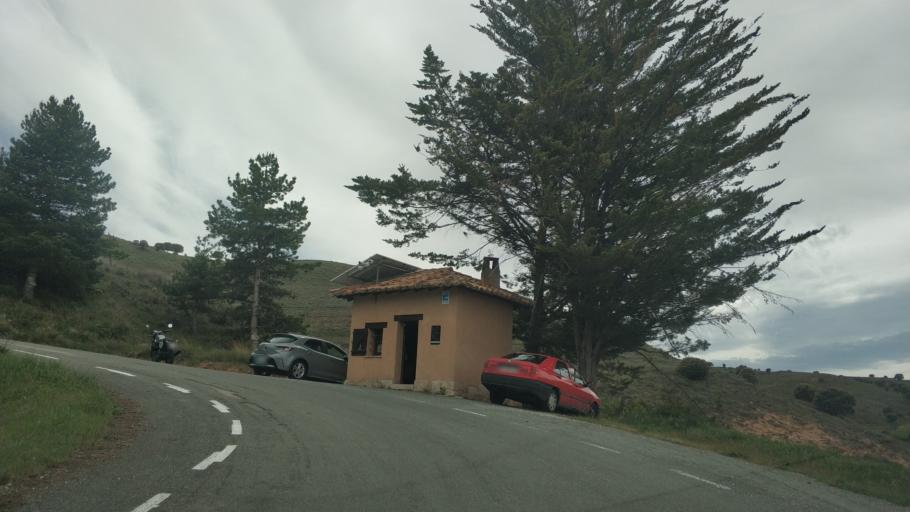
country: ES
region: Castille and Leon
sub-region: Provincia de Soria
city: Caltojar
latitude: 41.4185
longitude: -2.7908
